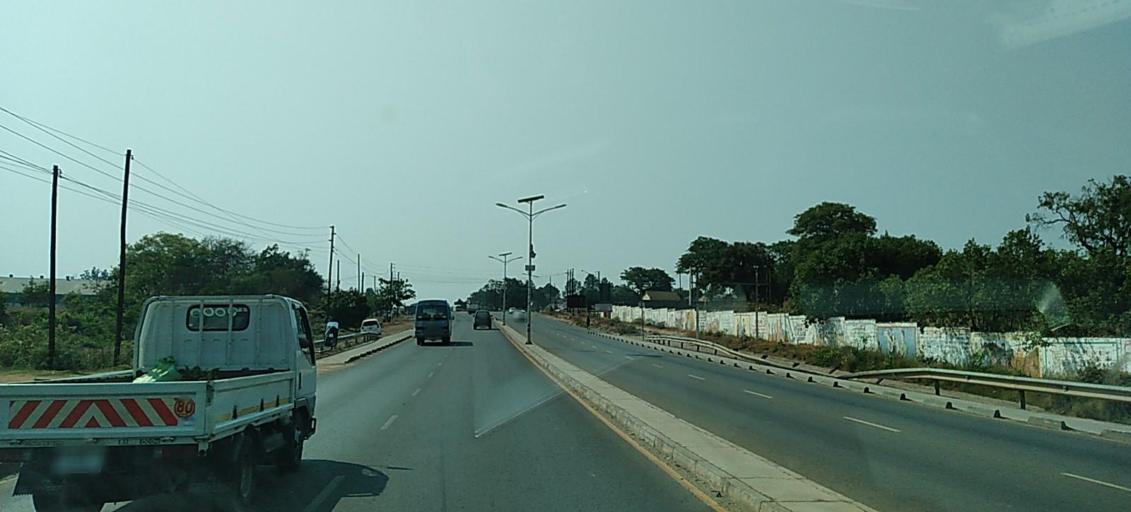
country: ZM
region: Copperbelt
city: Chingola
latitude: -12.5554
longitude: 27.8722
